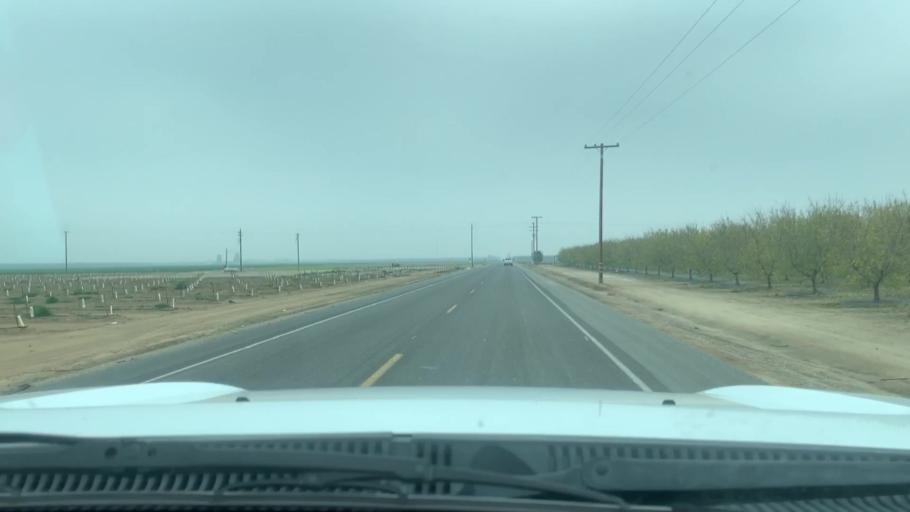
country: US
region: California
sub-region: Kern County
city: Wasco
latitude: 35.5002
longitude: -119.3880
